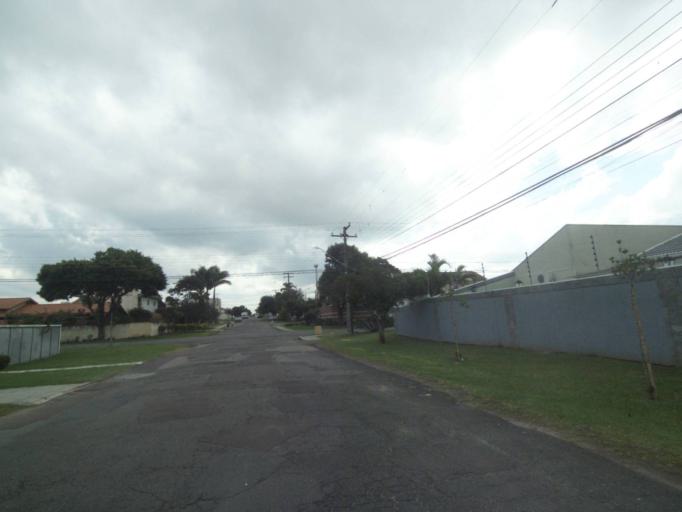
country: BR
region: Parana
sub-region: Pinhais
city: Pinhais
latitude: -25.4536
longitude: -49.2064
